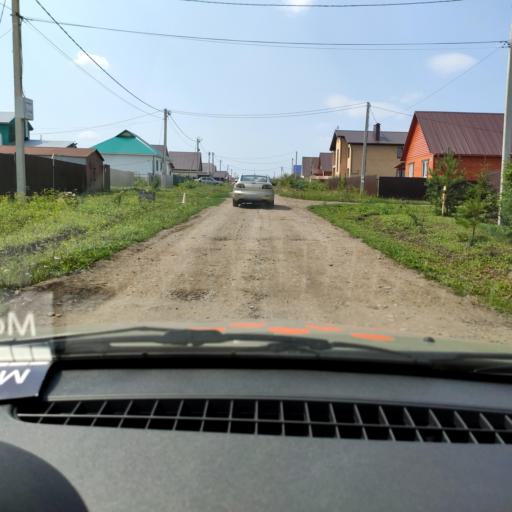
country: RU
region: Bashkortostan
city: Iglino
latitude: 54.8310
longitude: 56.4495
